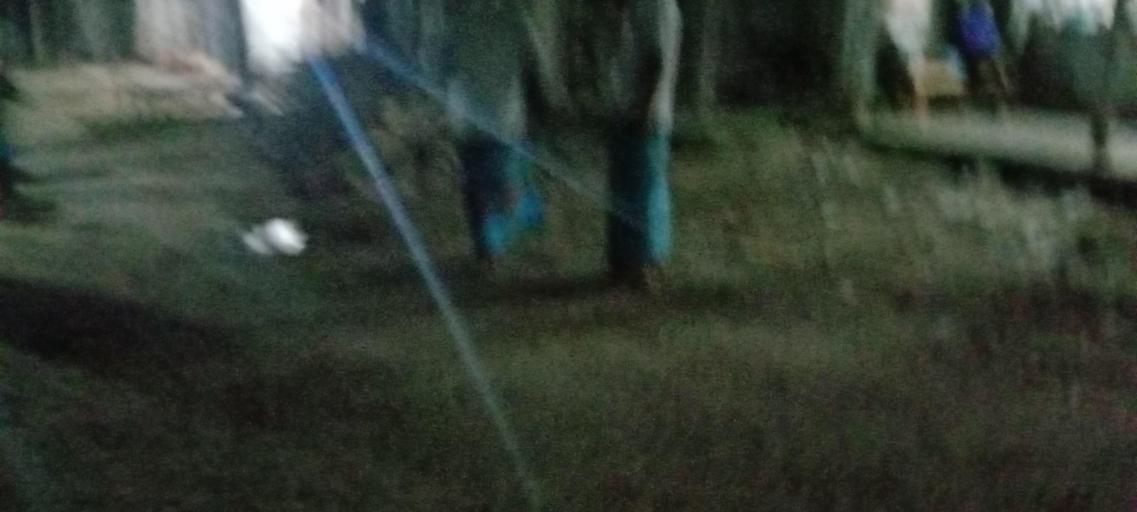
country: BD
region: Dhaka
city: Sakhipur
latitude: 24.4450
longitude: 90.3030
